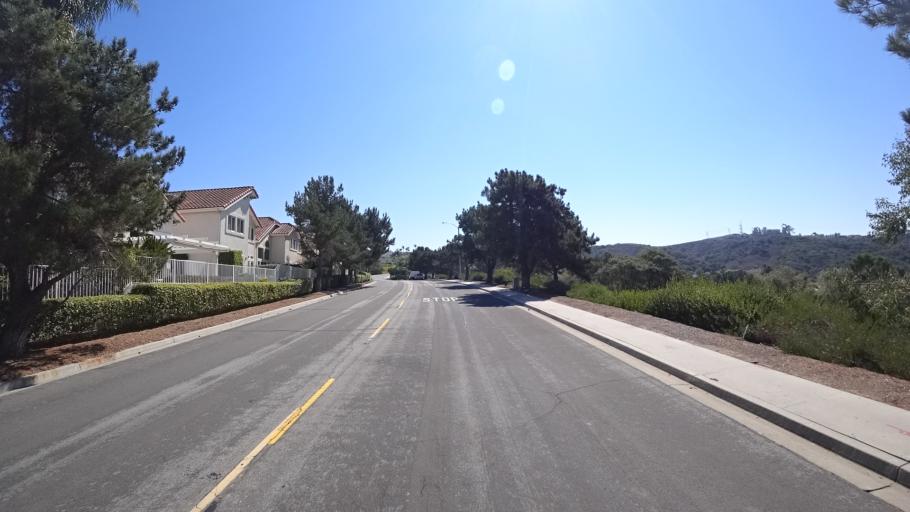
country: US
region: California
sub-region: Orange County
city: San Clemente
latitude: 33.4394
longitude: -117.5941
